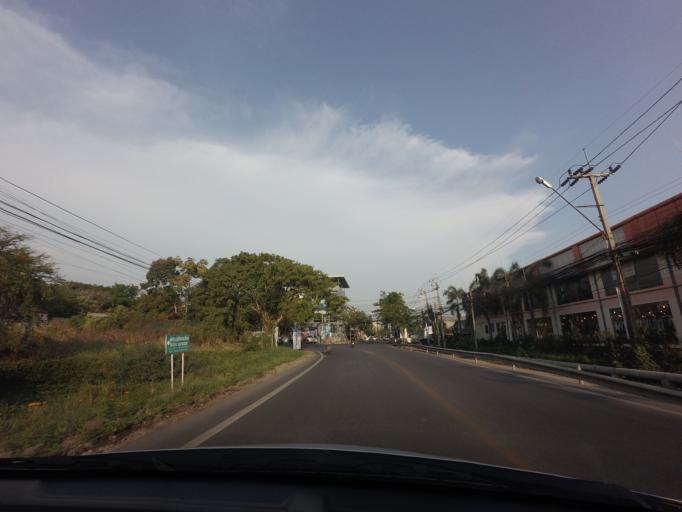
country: TH
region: Bangkok
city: Saphan Sung
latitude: 13.7392
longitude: 100.6923
